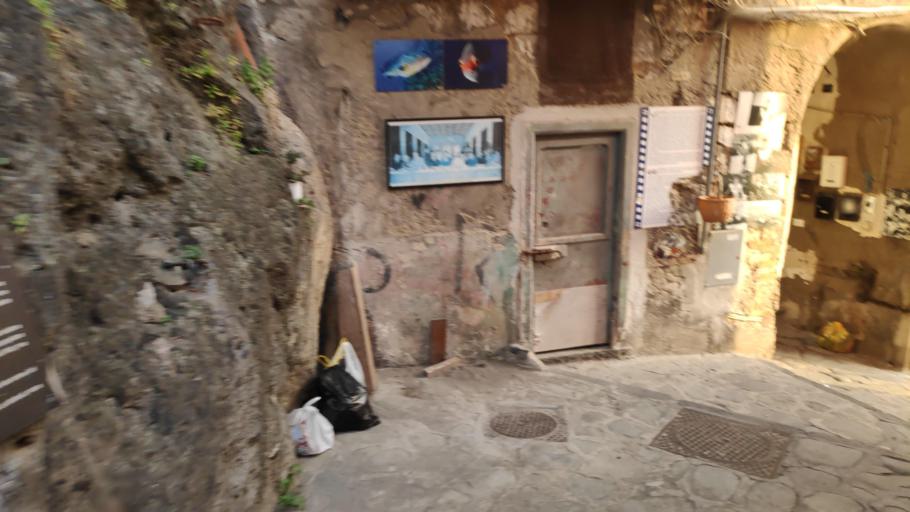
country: IT
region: Campania
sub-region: Provincia di Napoli
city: Sorrento
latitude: 40.6278
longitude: 14.3671
